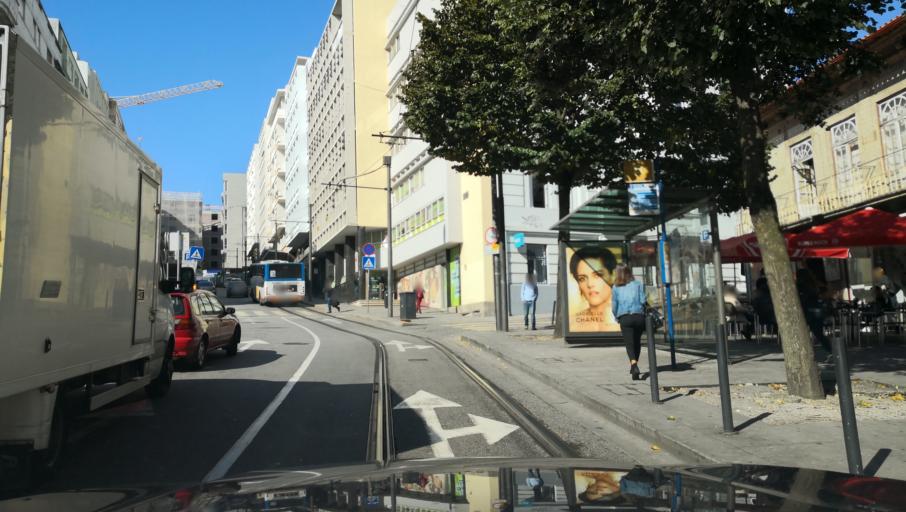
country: PT
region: Porto
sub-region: Porto
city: Porto
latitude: 41.1482
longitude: -8.6127
